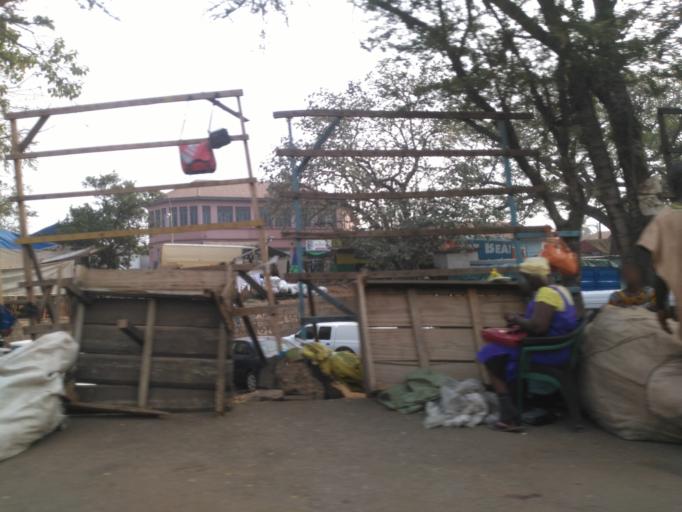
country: GH
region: Ashanti
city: Kumasi
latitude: 6.6914
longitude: -1.6183
